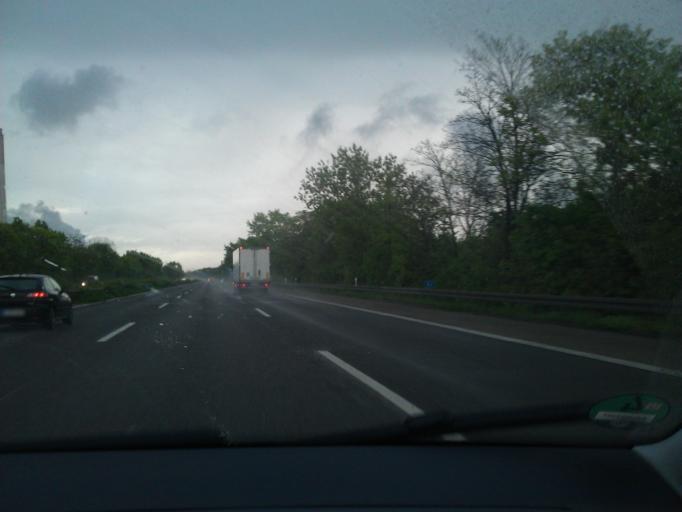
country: DE
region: North Rhine-Westphalia
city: Wesseling
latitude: 50.8342
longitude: 6.9654
